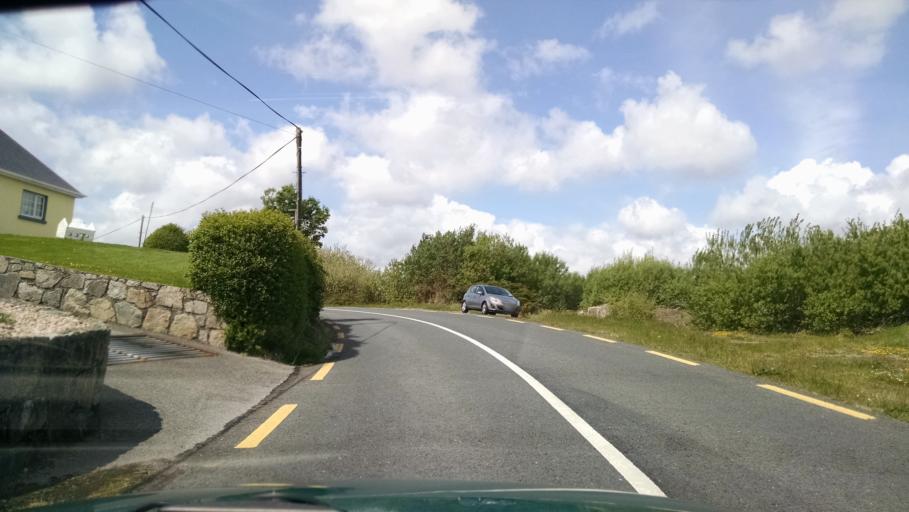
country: IE
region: Connaught
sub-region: County Galway
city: Oughterard
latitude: 53.3914
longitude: -9.6429
